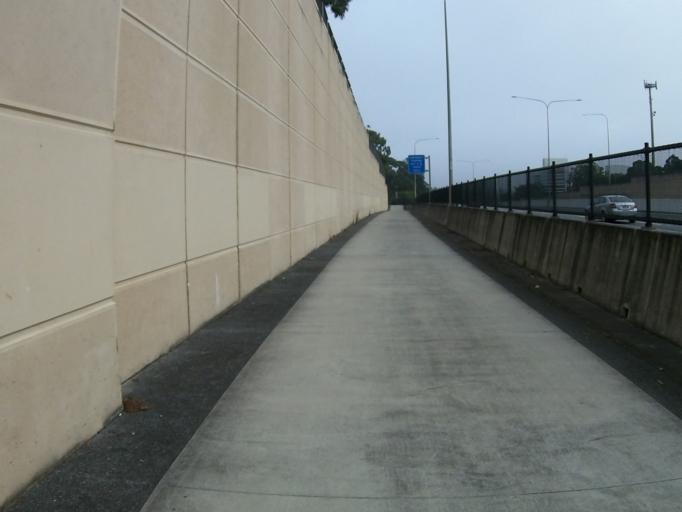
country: AU
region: Queensland
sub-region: Brisbane
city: Upper Mount Gravatt
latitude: -27.5643
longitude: 153.0806
